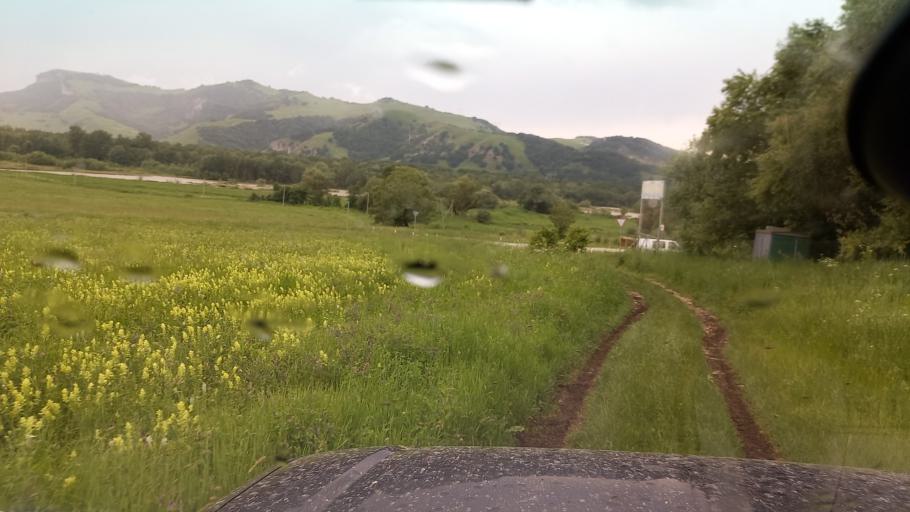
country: RU
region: Krasnodarskiy
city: Psebay
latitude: 44.1544
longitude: 40.8555
